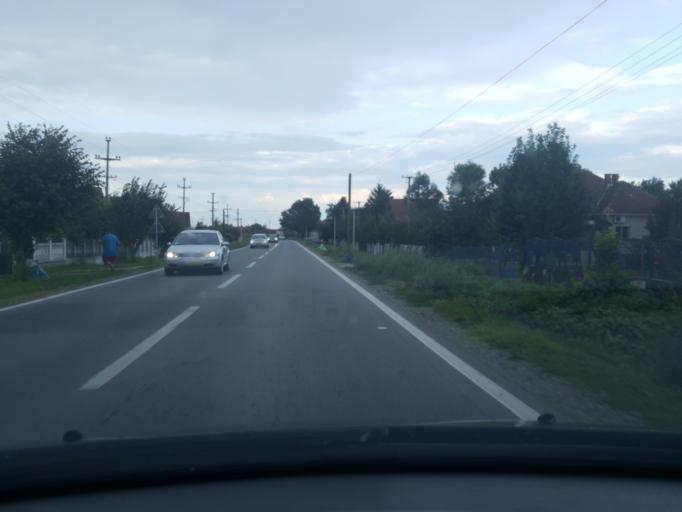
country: RS
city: Lipolist
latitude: 44.7334
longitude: 19.5102
